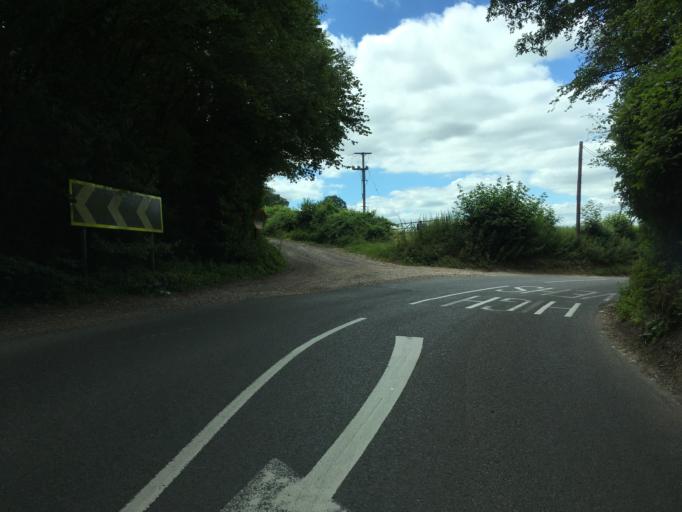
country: GB
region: England
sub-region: Hampshire
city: Highclere
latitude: 51.2402
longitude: -1.3714
